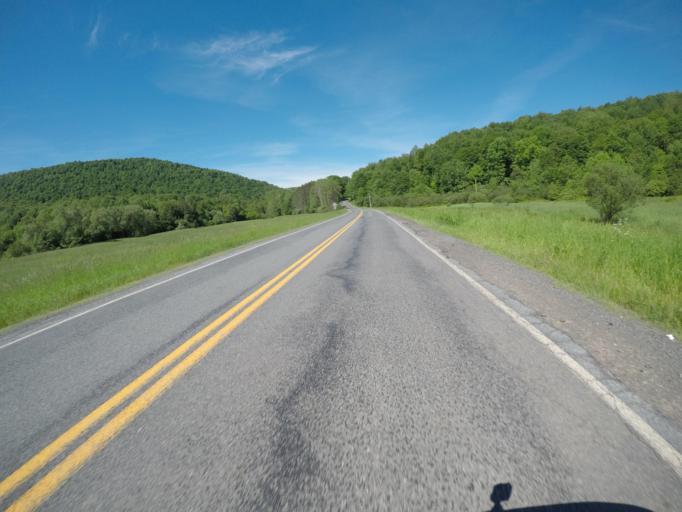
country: US
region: New York
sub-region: Delaware County
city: Delhi
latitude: 42.2157
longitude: -74.8928
